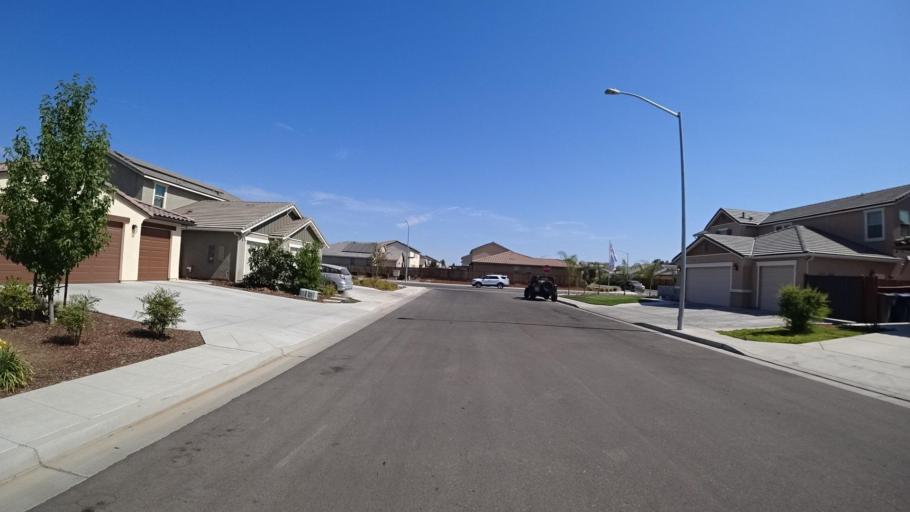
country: US
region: California
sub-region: Fresno County
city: Sunnyside
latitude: 36.7692
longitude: -119.6610
